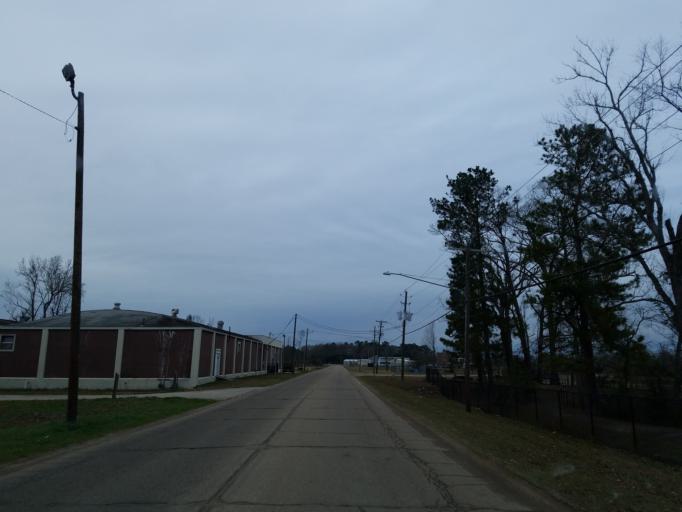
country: US
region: Mississippi
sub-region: Forrest County
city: Hattiesburg
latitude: 31.3108
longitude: -89.2807
